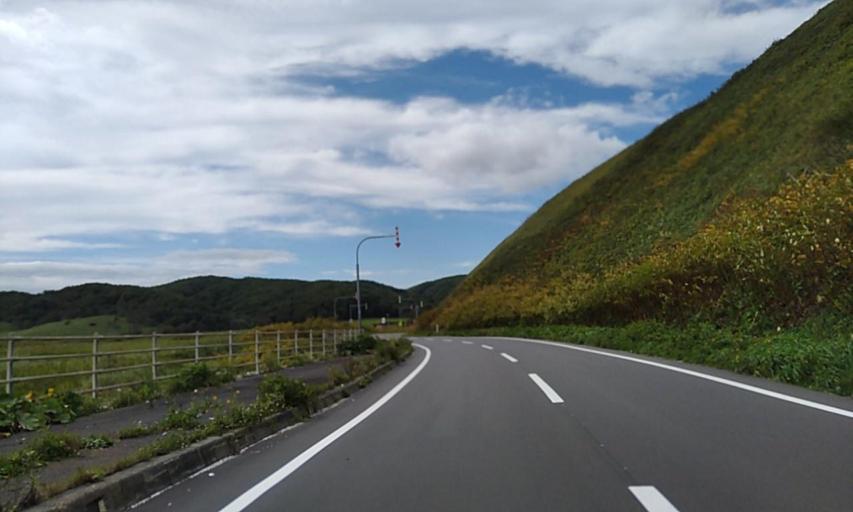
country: JP
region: Hokkaido
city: Kushiro
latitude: 42.7921
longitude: 143.8019
